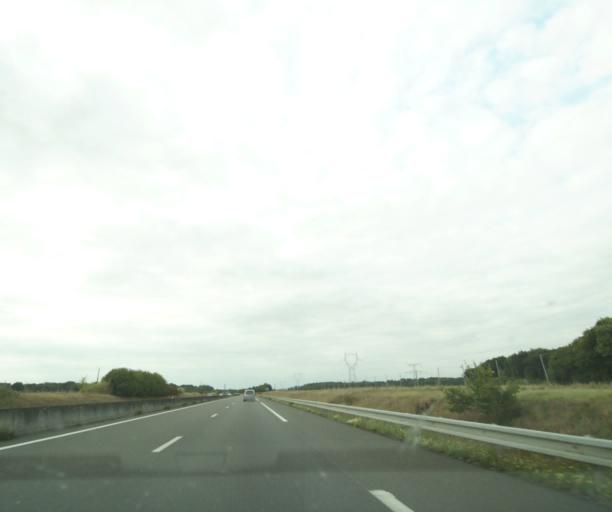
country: FR
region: Centre
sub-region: Departement d'Indre-et-Loire
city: Rouziers-de-Touraine
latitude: 47.5152
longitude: 0.6329
